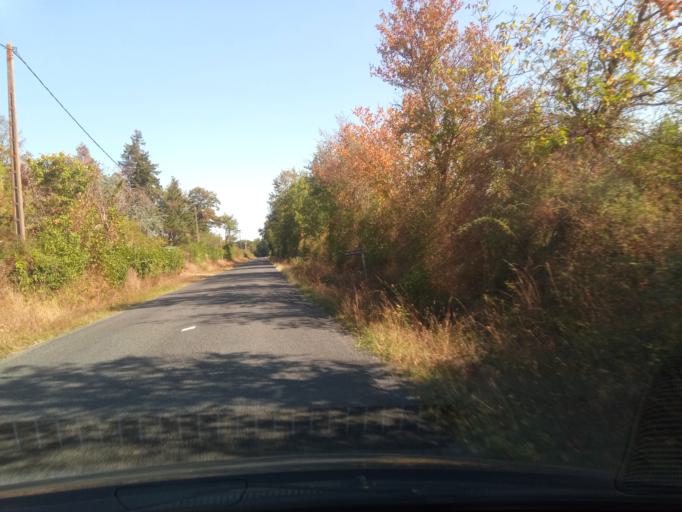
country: FR
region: Poitou-Charentes
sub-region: Departement de la Vienne
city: Saulge
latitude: 46.3663
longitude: 0.8806
